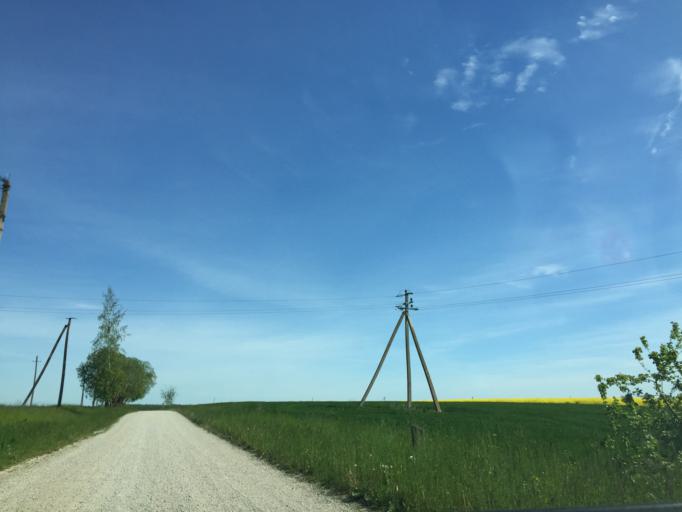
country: LT
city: Linkuva
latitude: 56.0710
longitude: 24.0640
